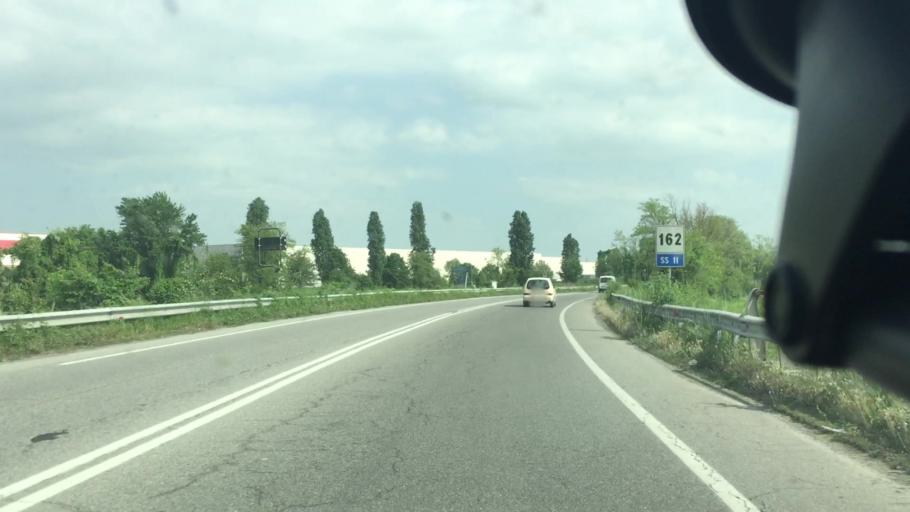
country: IT
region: Lombardy
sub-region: Citta metropolitana di Milano
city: Sant'Agata Martesana
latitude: 45.5242
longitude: 9.3927
